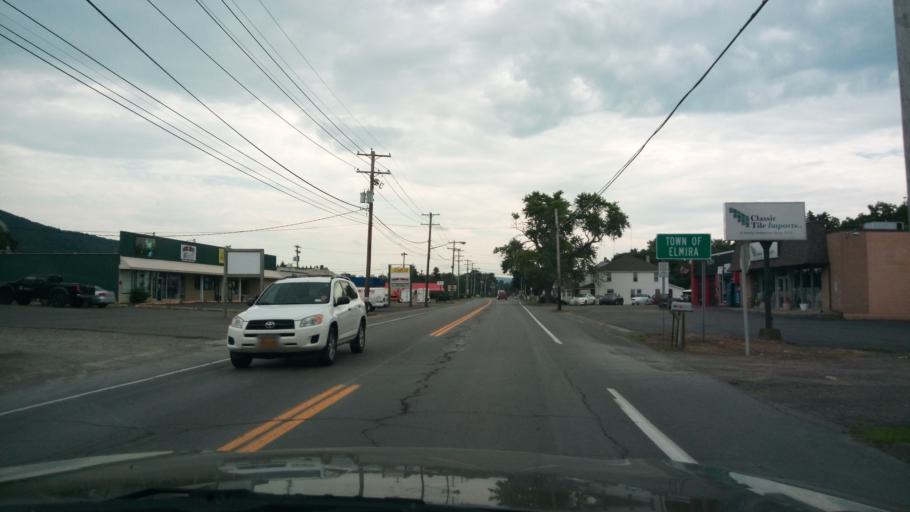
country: US
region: New York
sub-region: Chemung County
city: Elmira Heights
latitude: 42.1251
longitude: -76.8101
